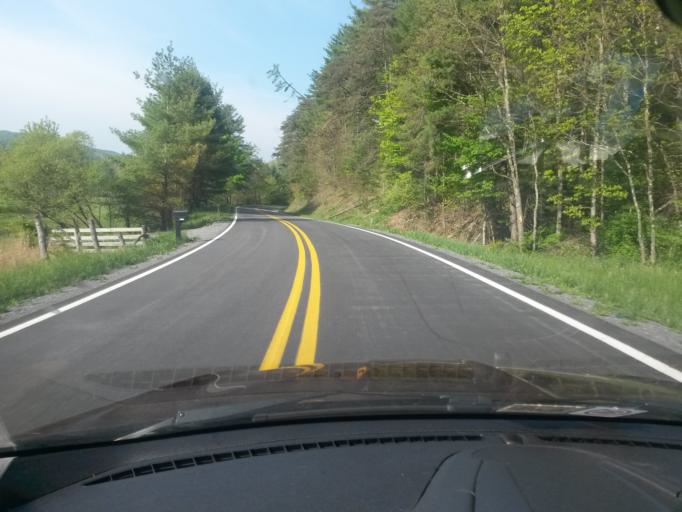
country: US
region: West Virginia
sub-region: Pocahontas County
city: Marlinton
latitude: 38.0061
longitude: -80.0677
